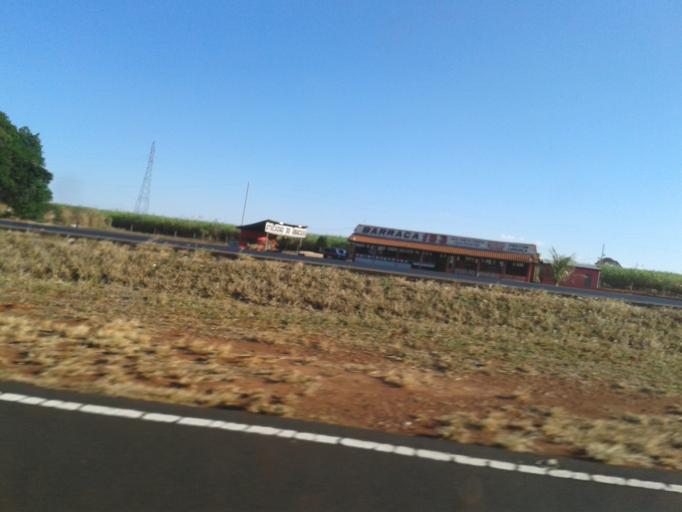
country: BR
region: Minas Gerais
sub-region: Centralina
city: Centralina
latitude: -18.7144
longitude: -49.1319
